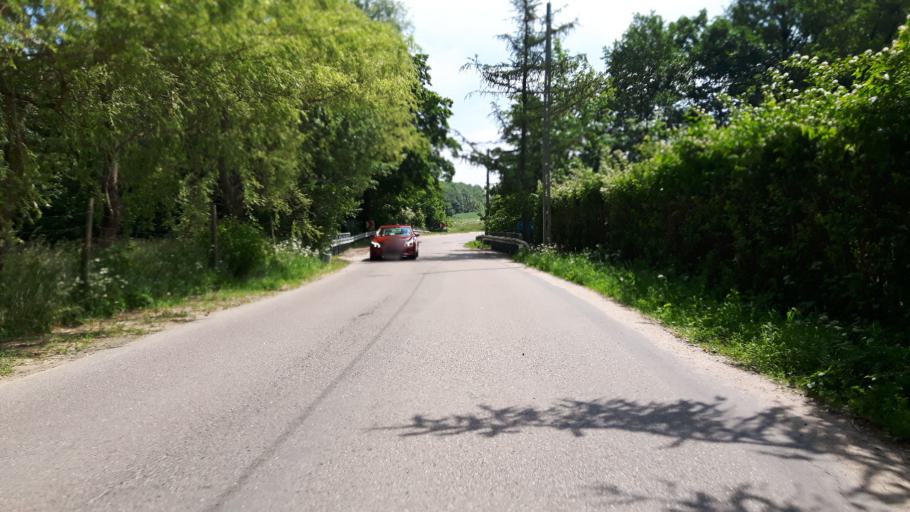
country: PL
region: Pomeranian Voivodeship
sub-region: Powiat wejherowski
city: Choczewo
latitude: 54.7555
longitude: 17.7904
